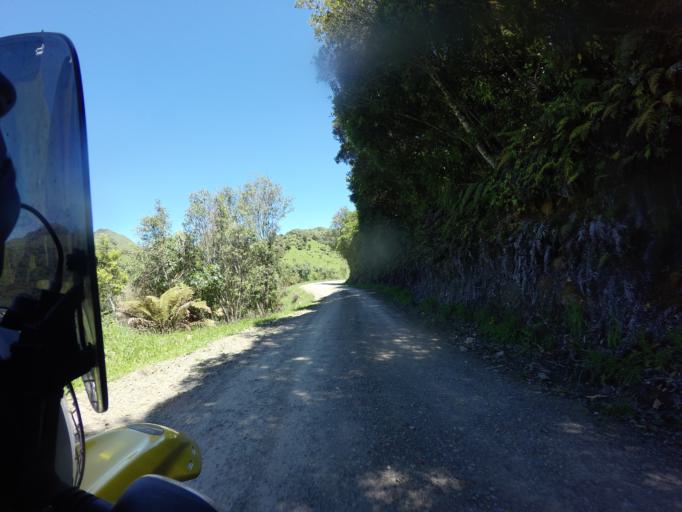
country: NZ
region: Bay of Plenty
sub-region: Opotiki District
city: Opotiki
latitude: -38.4079
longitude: 177.4376
